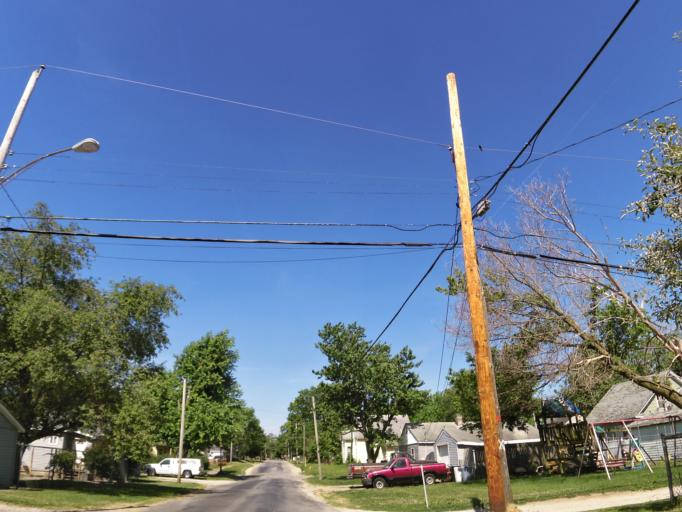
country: US
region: Illinois
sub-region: Vermilion County
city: Danville
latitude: 40.1338
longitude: -87.5825
